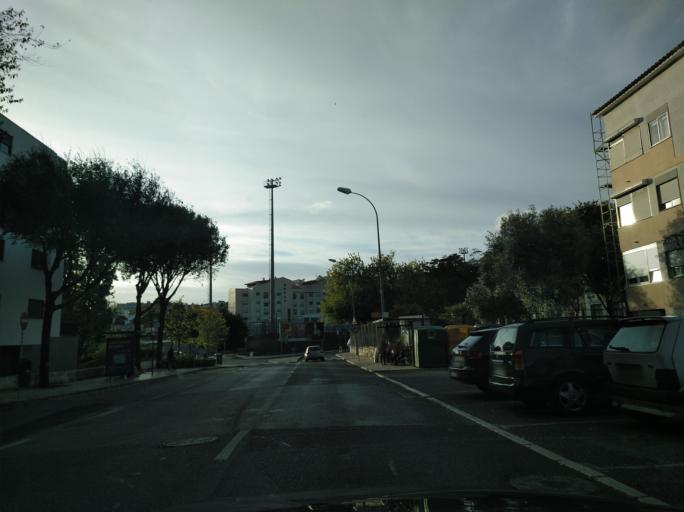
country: PT
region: Lisbon
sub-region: Oeiras
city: Linda-a-Velha
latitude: 38.7223
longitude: -9.2243
